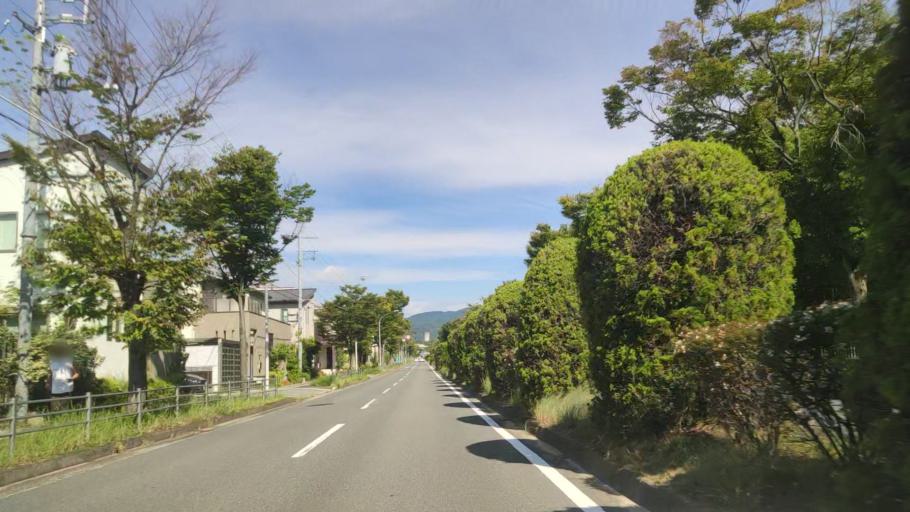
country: JP
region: Osaka
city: Mino
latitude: 34.8142
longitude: 135.5143
